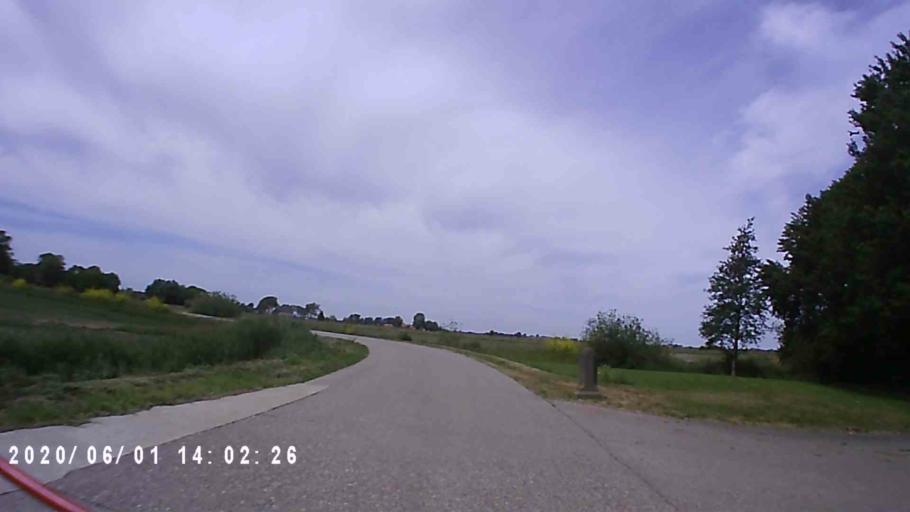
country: NL
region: Friesland
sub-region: Gemeente Littenseradiel
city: Winsum
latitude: 53.1114
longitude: 5.6415
